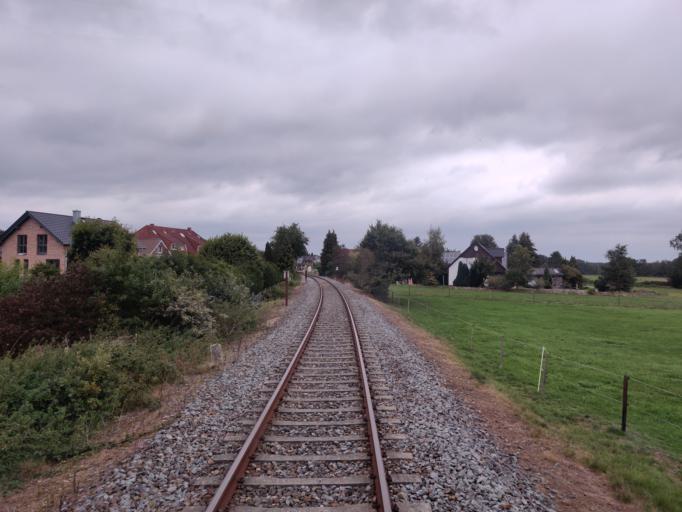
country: DE
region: Lower Saxony
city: Gnarrenburg
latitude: 53.3919
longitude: 9.0153
